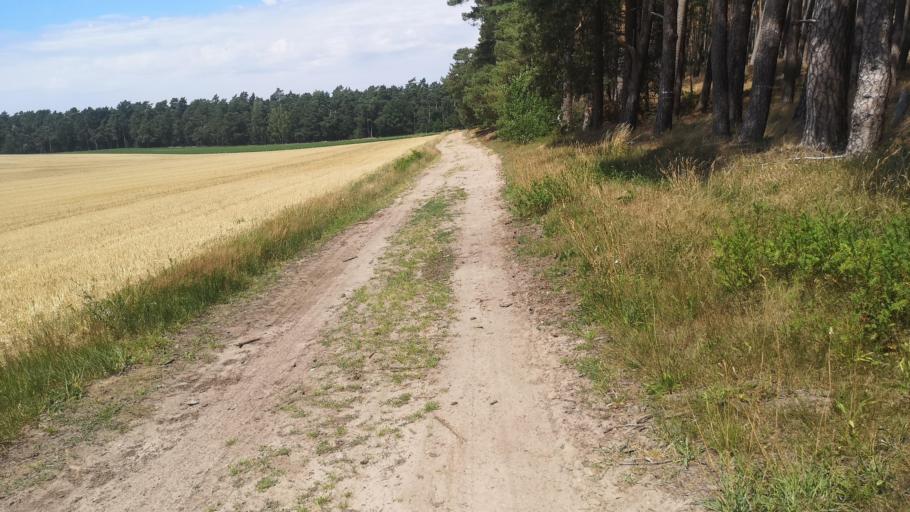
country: DE
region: Lower Saxony
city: Dahlem
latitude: 53.2258
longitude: 10.7246
